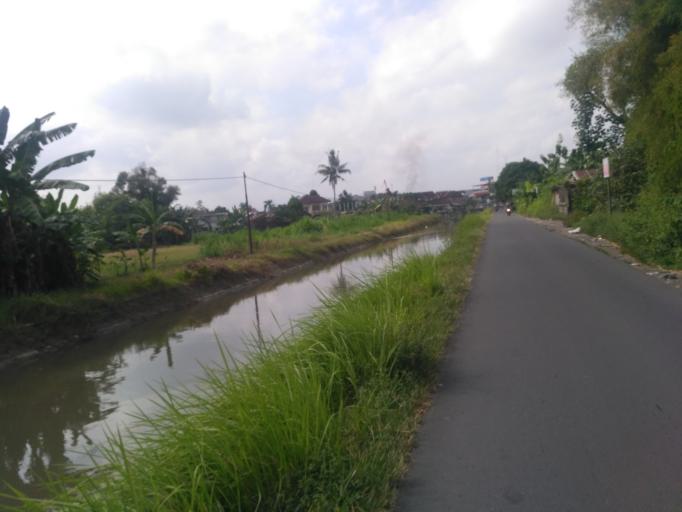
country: ID
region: Daerah Istimewa Yogyakarta
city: Yogyakarta
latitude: -7.7593
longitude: 110.3592
